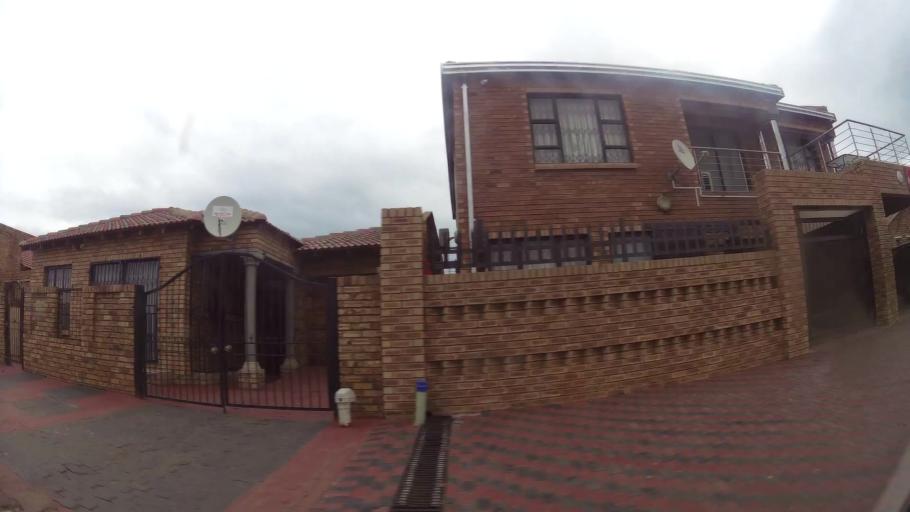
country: ZA
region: Gauteng
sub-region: Ekurhuleni Metropolitan Municipality
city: Germiston
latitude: -26.3855
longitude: 28.1575
